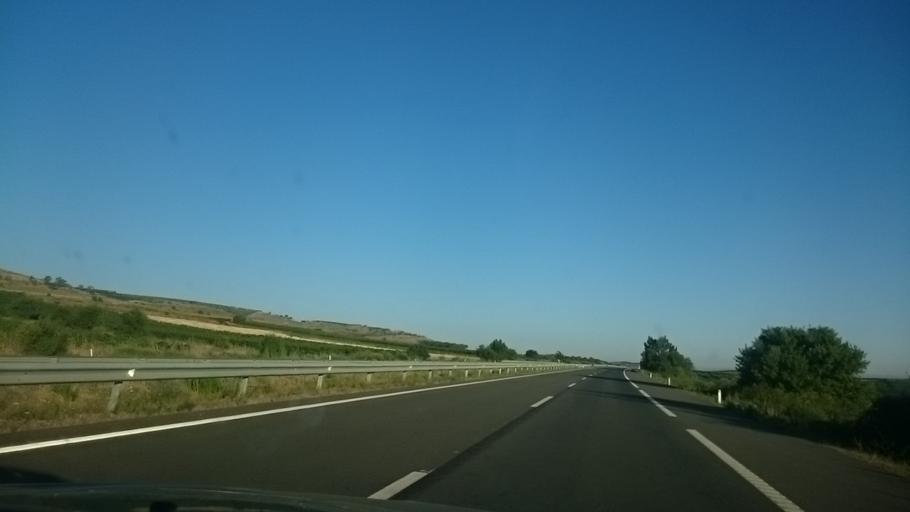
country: ES
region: La Rioja
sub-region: Provincia de La Rioja
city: Alcanadre
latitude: 42.3821
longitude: -2.1135
